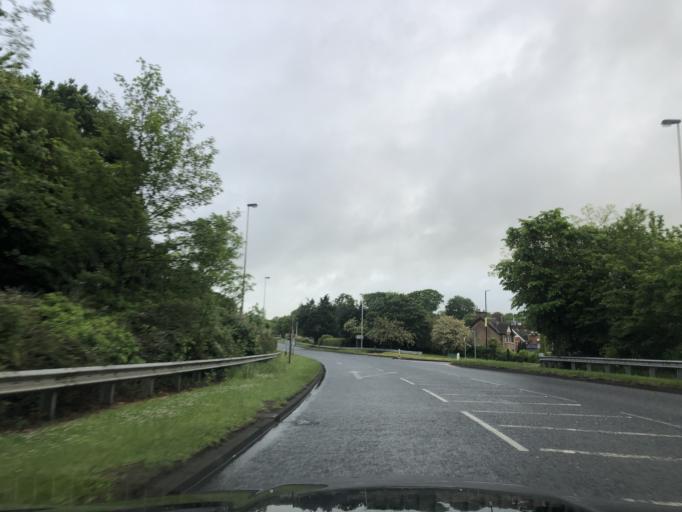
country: GB
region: Northern Ireland
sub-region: Antrim Borough
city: Antrim
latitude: 54.7117
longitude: -6.2198
